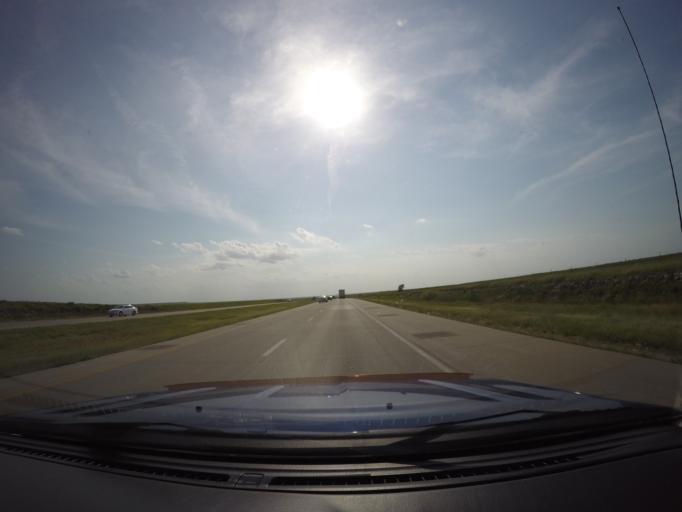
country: US
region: Kansas
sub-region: Wabaunsee County
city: Alma
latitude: 39.0655
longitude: -96.4140
